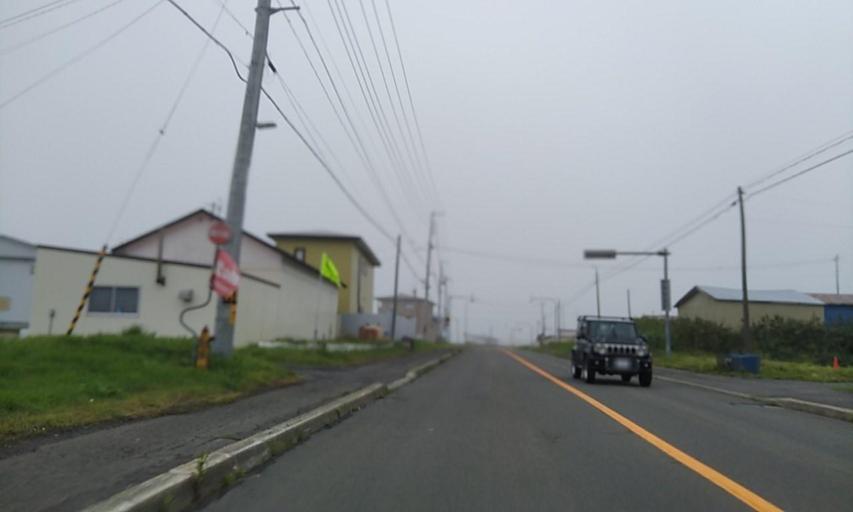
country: JP
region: Hokkaido
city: Nemuro
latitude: 43.3287
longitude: 145.6893
